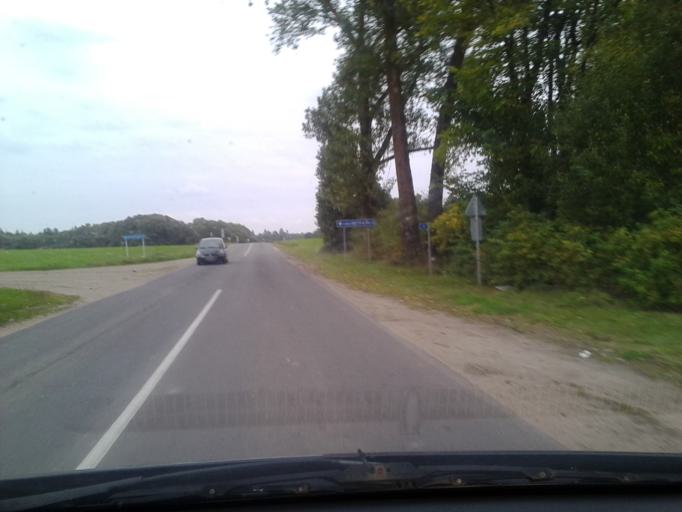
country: BY
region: Vitebsk
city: Pastavy
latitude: 55.1310
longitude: 26.9375
